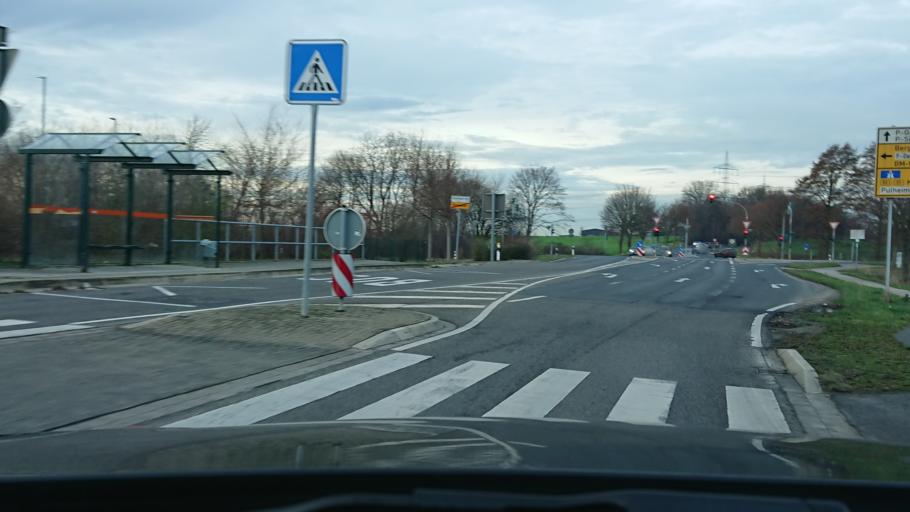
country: DE
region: North Rhine-Westphalia
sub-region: Regierungsbezirk Koln
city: Pulheim
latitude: 50.9655
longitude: 6.7795
